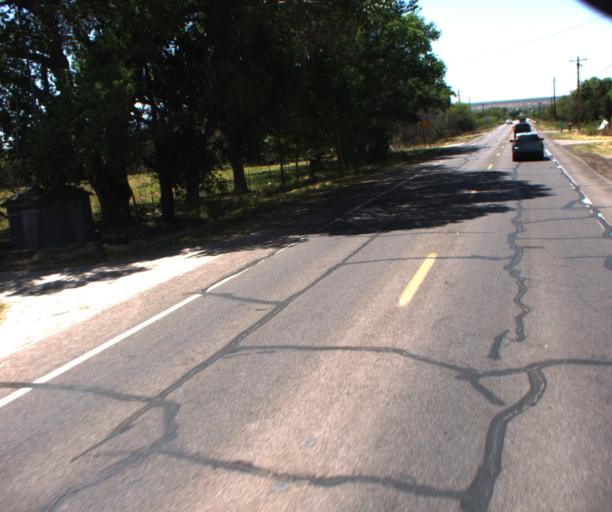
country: US
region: Arizona
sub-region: Cochise County
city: Saint David
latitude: 31.9054
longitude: -110.2423
